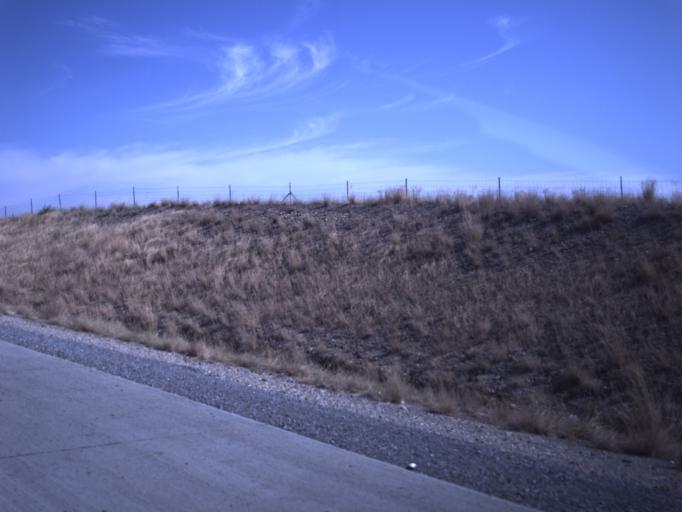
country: US
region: Utah
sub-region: Salt Lake County
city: Oquirrh
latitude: 40.6171
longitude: -112.0406
